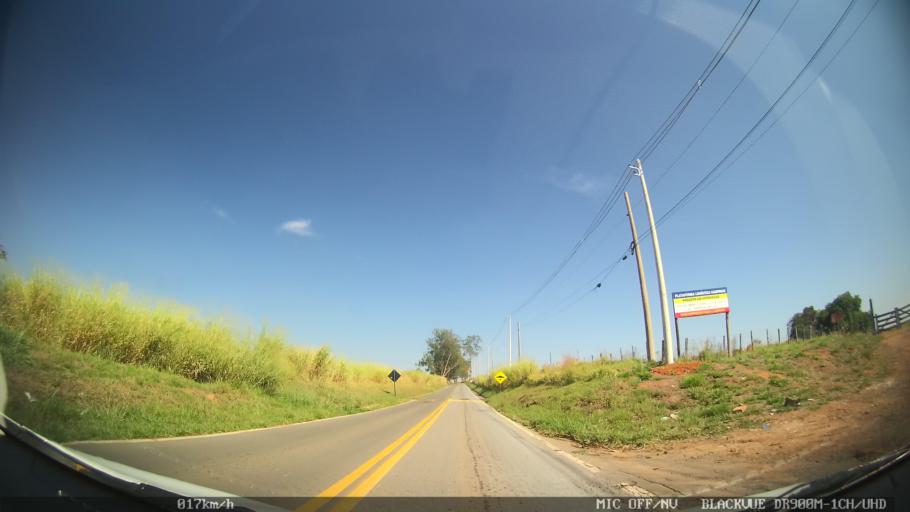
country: BR
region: Sao Paulo
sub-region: Valinhos
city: Valinhos
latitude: -23.0211
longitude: -47.0976
